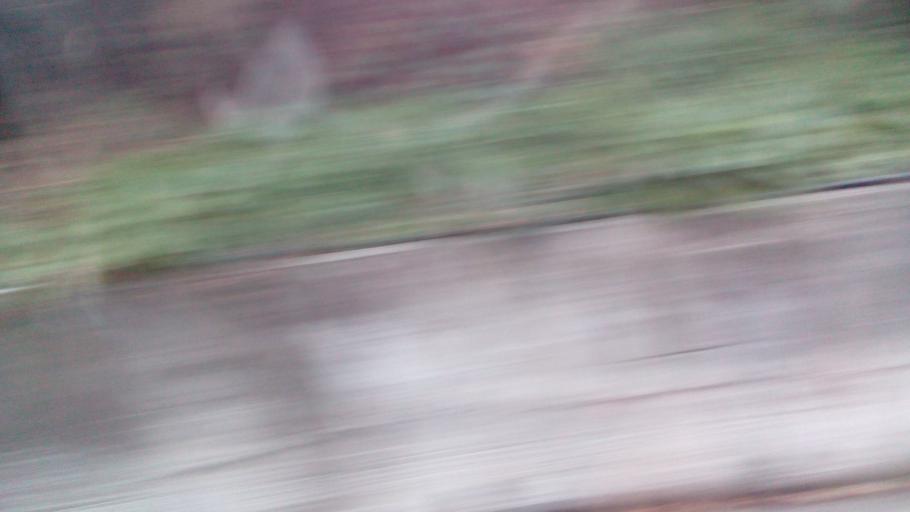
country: TW
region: Taiwan
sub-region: Hualien
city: Hualian
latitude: 24.3279
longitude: 121.2965
